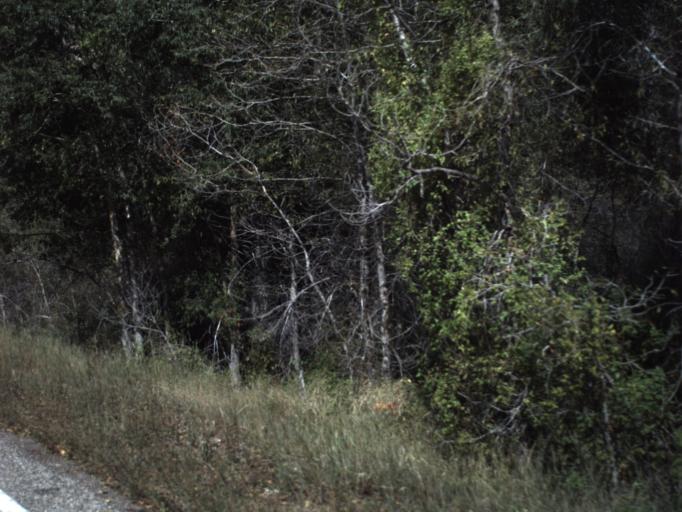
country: US
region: Utah
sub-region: Beaver County
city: Beaver
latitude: 38.2656
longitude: -112.5483
